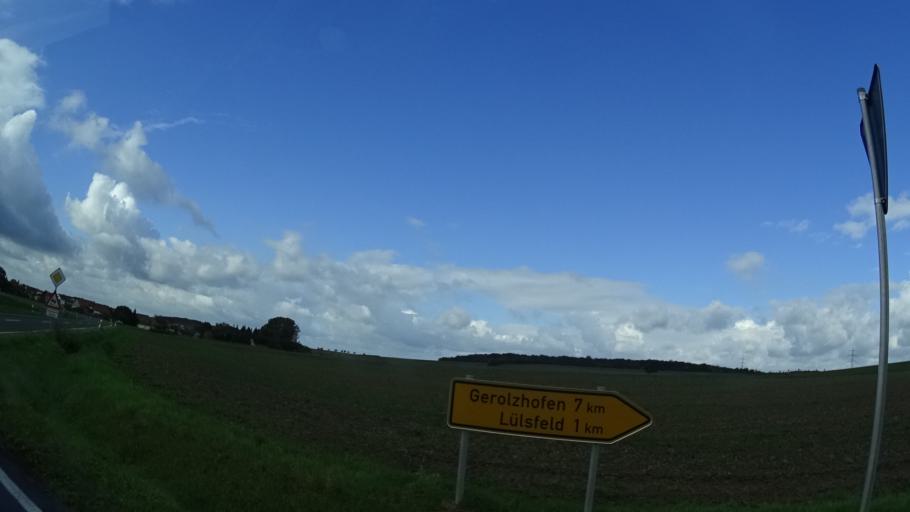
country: DE
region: Bavaria
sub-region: Regierungsbezirk Unterfranken
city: Frankenwinheim
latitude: 49.8613
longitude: 10.3008
